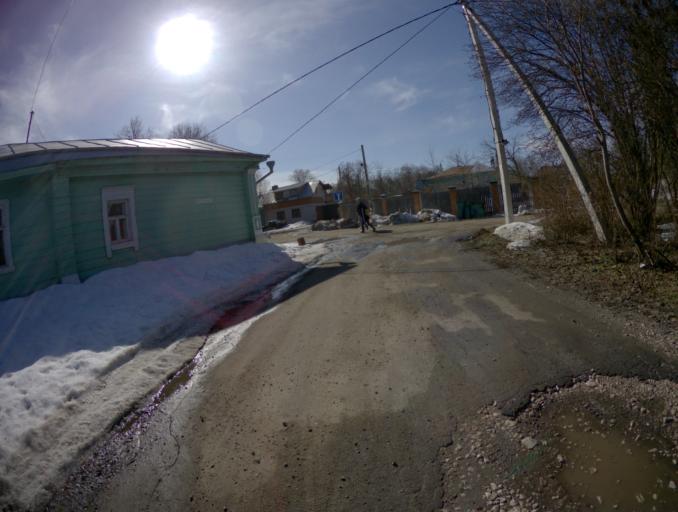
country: RU
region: Vladimir
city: Suzdal'
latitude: 56.4208
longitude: 40.4535
